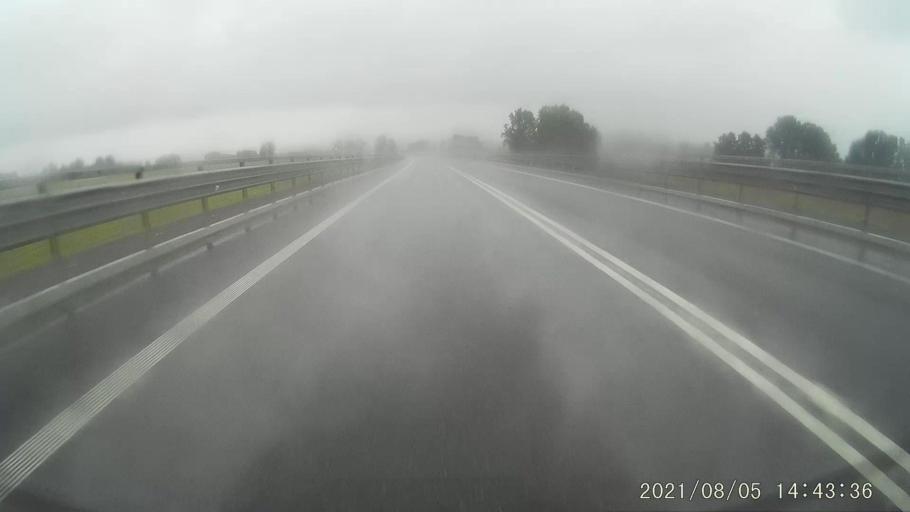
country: PL
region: Opole Voivodeship
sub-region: Powiat nyski
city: Nysa
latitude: 50.4854
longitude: 17.3881
